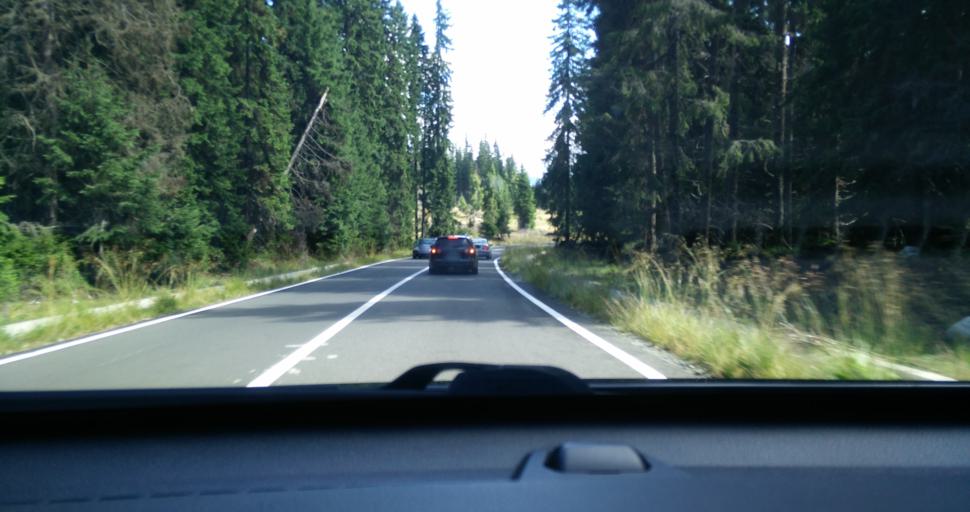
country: RO
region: Hunedoara
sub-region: Oras Petrila
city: Petrila
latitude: 45.4826
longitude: 23.6366
